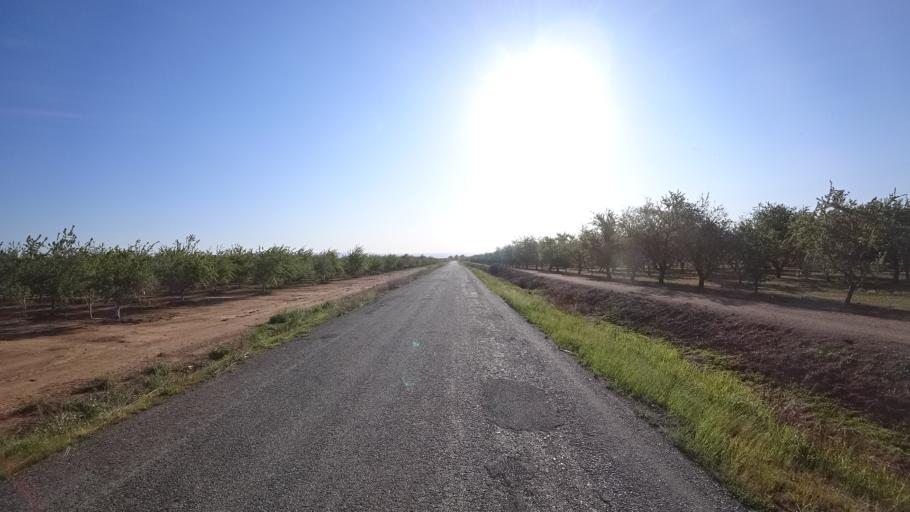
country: US
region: California
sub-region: Glenn County
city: Orland
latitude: 39.7976
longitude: -122.1370
